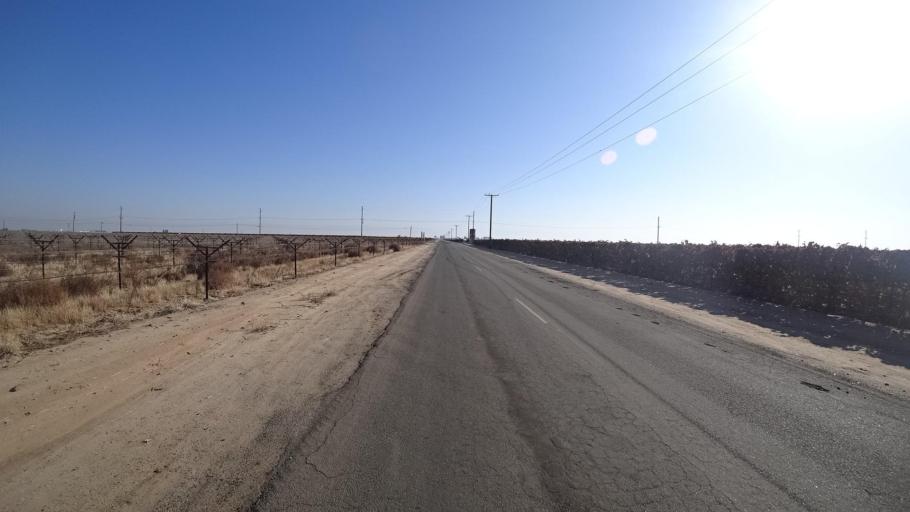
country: US
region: California
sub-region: Kern County
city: Delano
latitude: 35.7472
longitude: -119.2070
